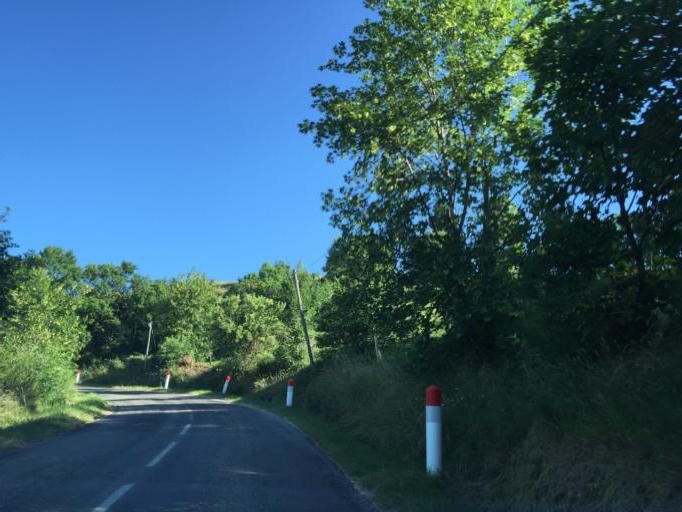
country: FR
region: Rhone-Alpes
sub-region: Departement de la Loire
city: Saint-Chamond
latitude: 45.4045
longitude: 4.5297
